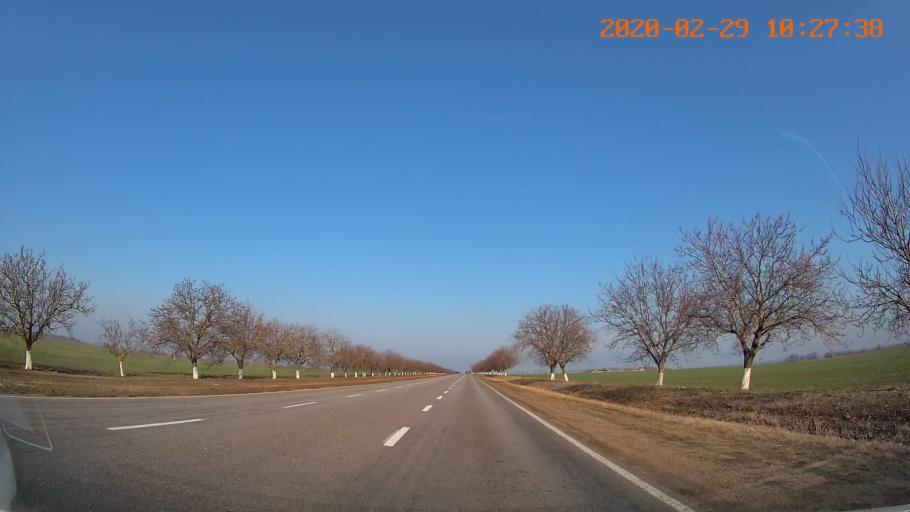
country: MD
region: Telenesti
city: Tiraspolul Nou
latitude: 46.8988
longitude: 29.5965
